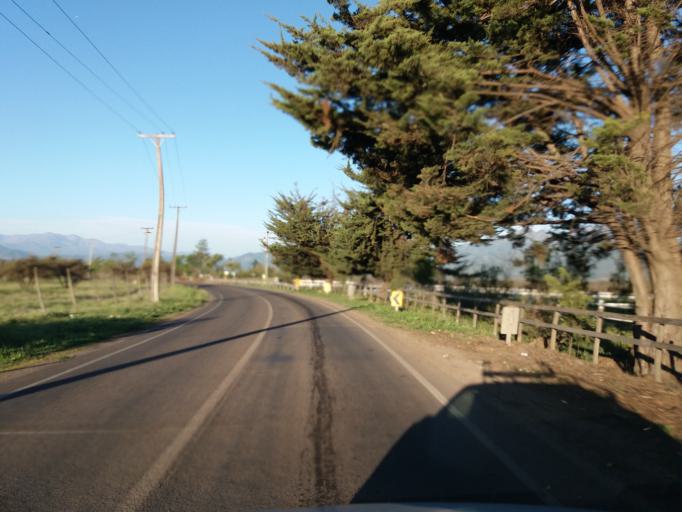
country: CL
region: Valparaiso
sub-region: Provincia de Quillota
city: Quillota
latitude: -32.9158
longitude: -71.3168
